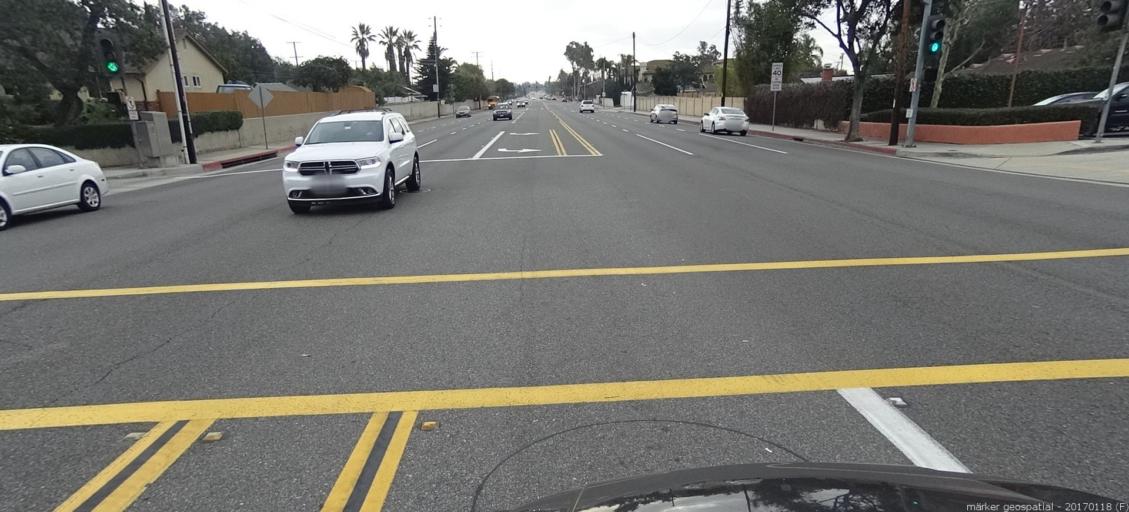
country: US
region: California
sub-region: Orange County
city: Tustin
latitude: 33.7469
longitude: -117.8074
